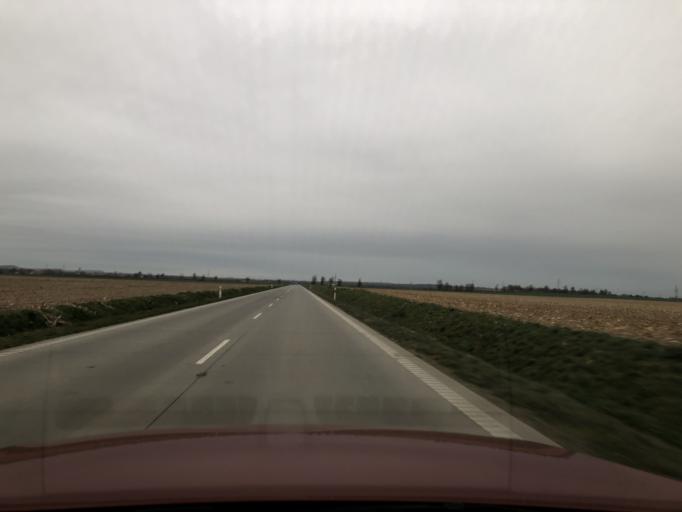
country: PL
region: Lower Silesian Voivodeship
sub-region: Powiat swidnicki
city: Zarow
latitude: 50.9198
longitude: 16.4776
